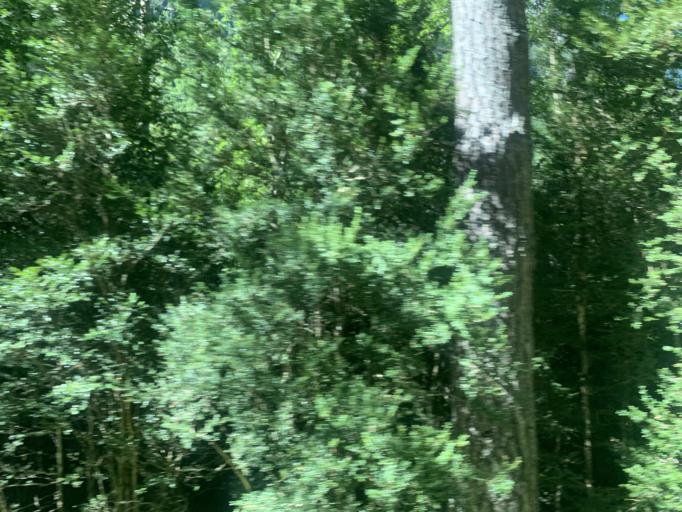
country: ES
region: Aragon
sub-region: Provincia de Huesca
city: Broto
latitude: 42.6507
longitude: -0.0661
